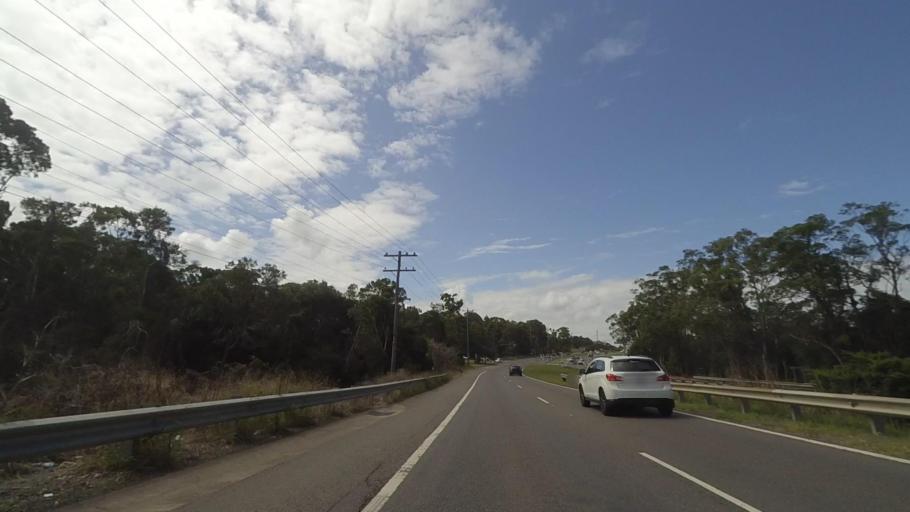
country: AU
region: New South Wales
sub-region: Lake Macquarie Shire
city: Windale
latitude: -33.0008
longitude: 151.6858
